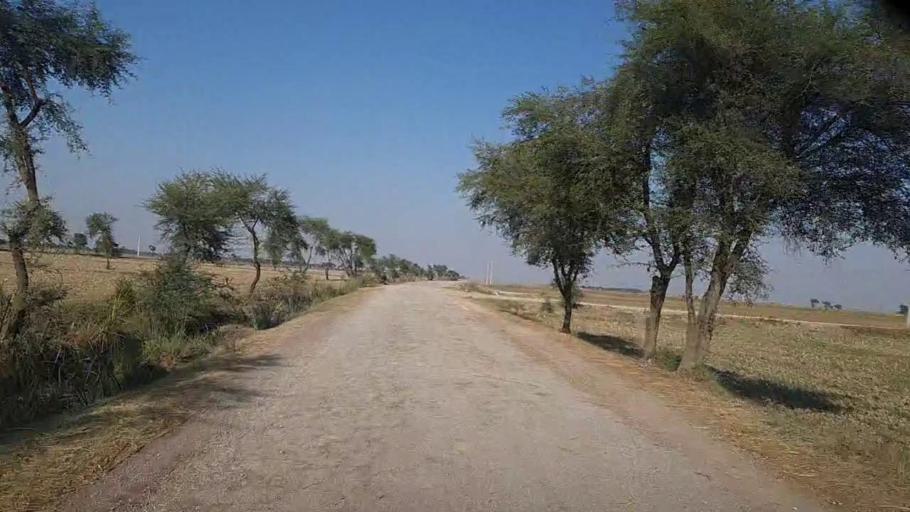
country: PK
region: Sindh
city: Thul
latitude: 28.3589
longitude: 68.7662
